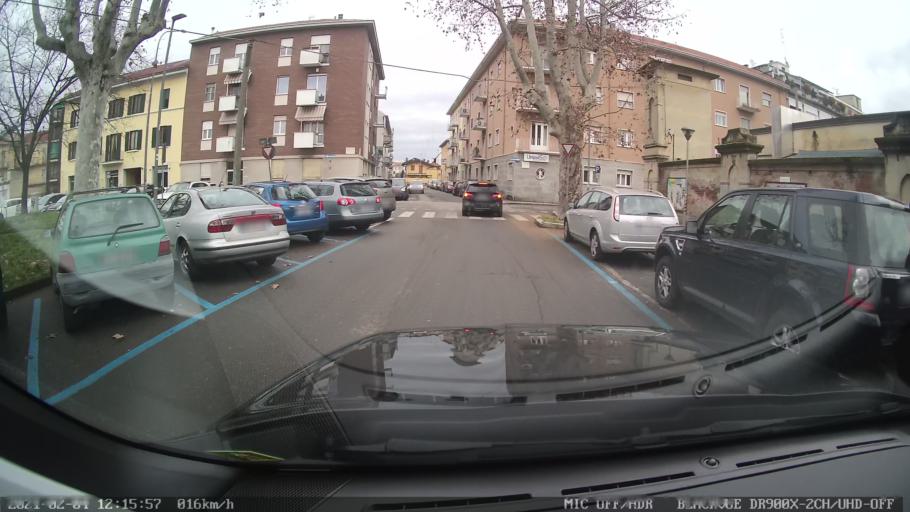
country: IT
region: Piedmont
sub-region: Provincia di Novara
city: Novara
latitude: 45.4488
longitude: 8.6113
